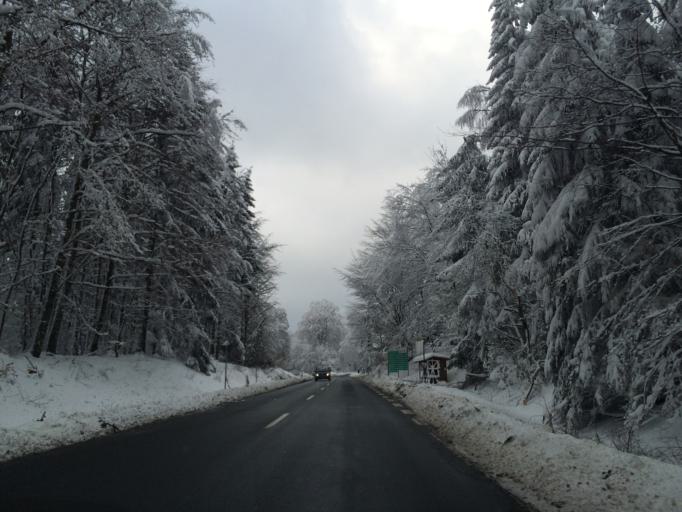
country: DE
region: Hesse
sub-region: Regierungsbezirk Darmstadt
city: Glashutten
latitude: 50.2242
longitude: 8.4362
